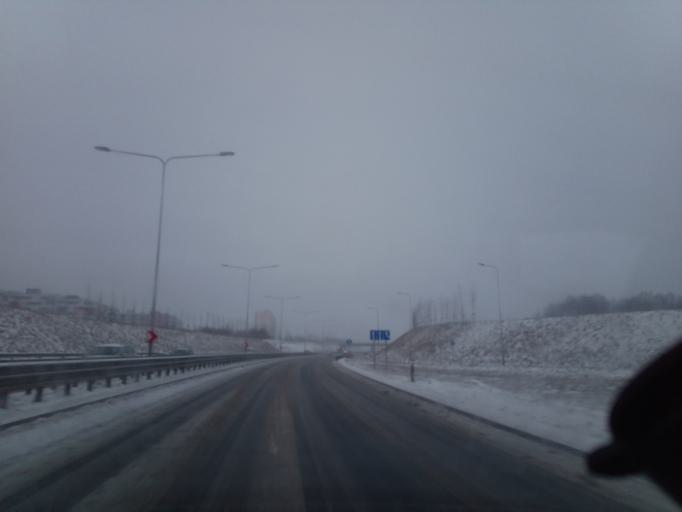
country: LT
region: Vilnius County
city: Pasilaiciai
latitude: 54.7424
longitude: 25.2172
